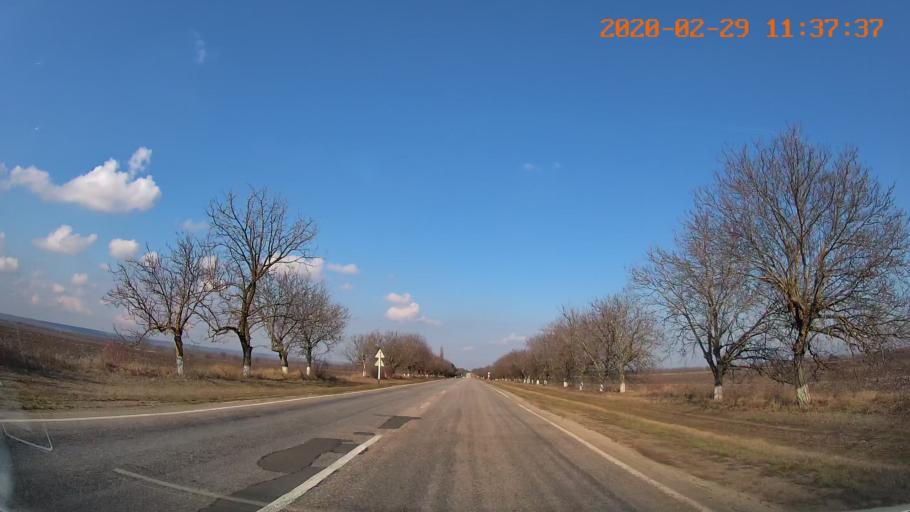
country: MD
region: Rezina
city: Saharna
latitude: 47.6142
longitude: 29.0445
